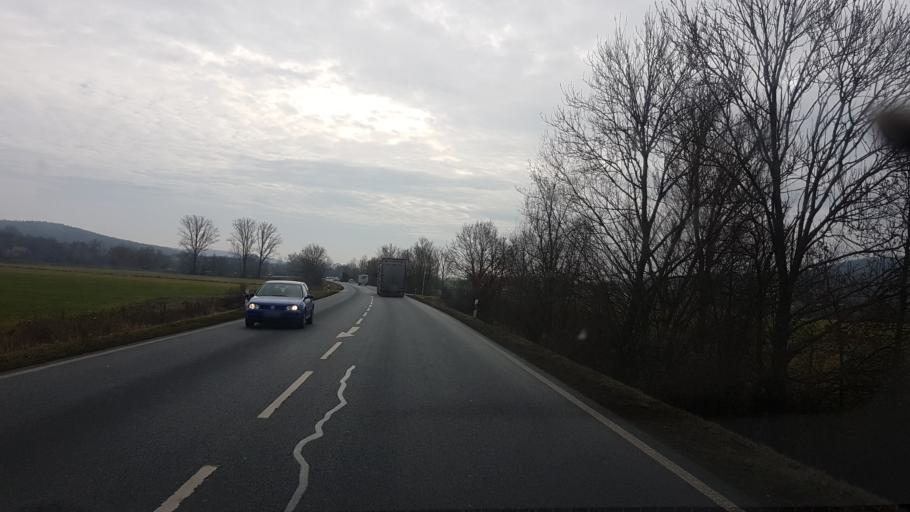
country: DE
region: Bavaria
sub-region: Regierungsbezirk Unterfranken
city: Rentweinsdorf
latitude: 50.0876
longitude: 10.7890
